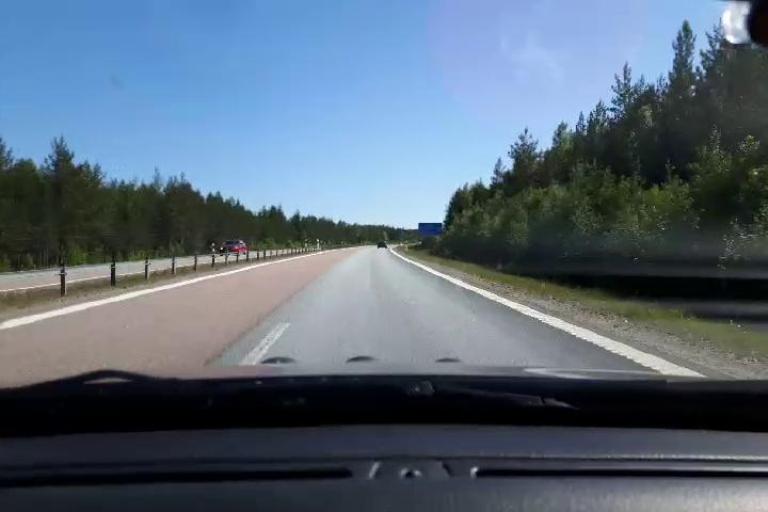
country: SE
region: Gaevleborg
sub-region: Soderhamns Kommun
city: Soderhamn
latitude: 61.4114
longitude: 16.9921
